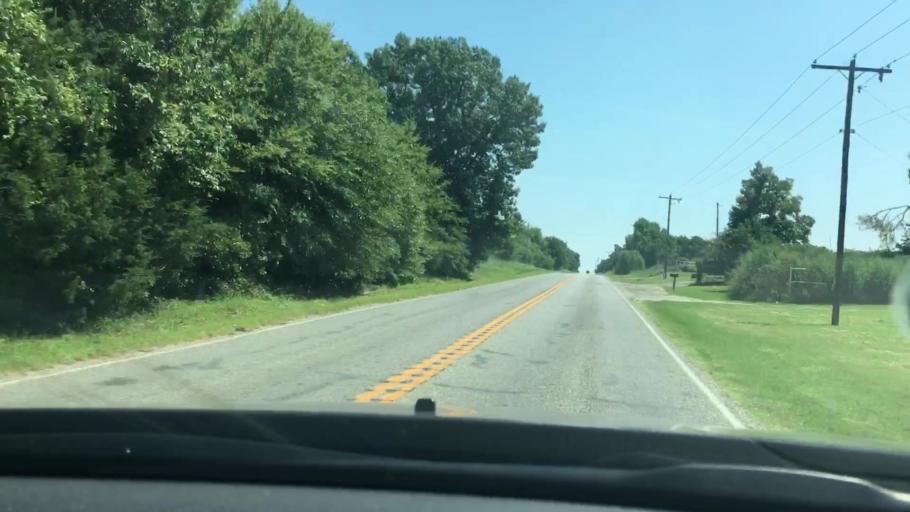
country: US
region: Oklahoma
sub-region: Johnston County
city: Tishomingo
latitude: 34.2377
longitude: -96.6064
